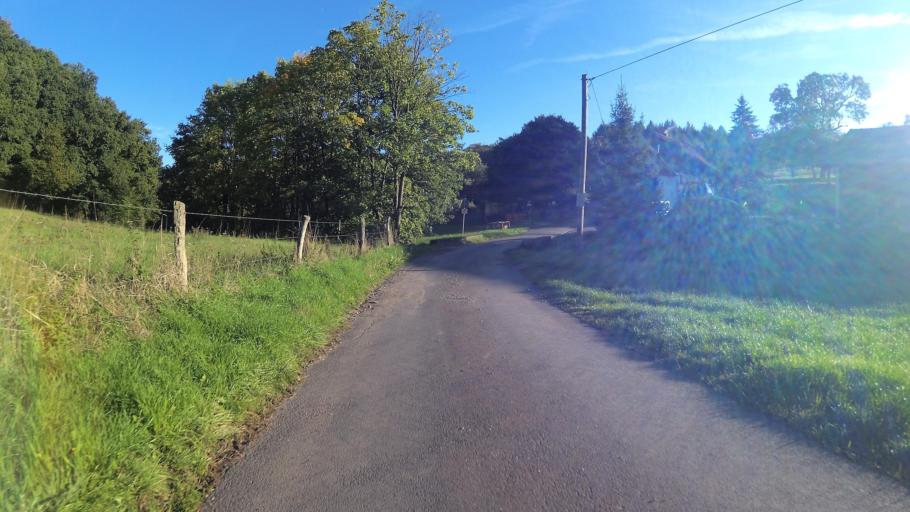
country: DE
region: Saarland
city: Freisen
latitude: 49.5098
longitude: 7.2221
